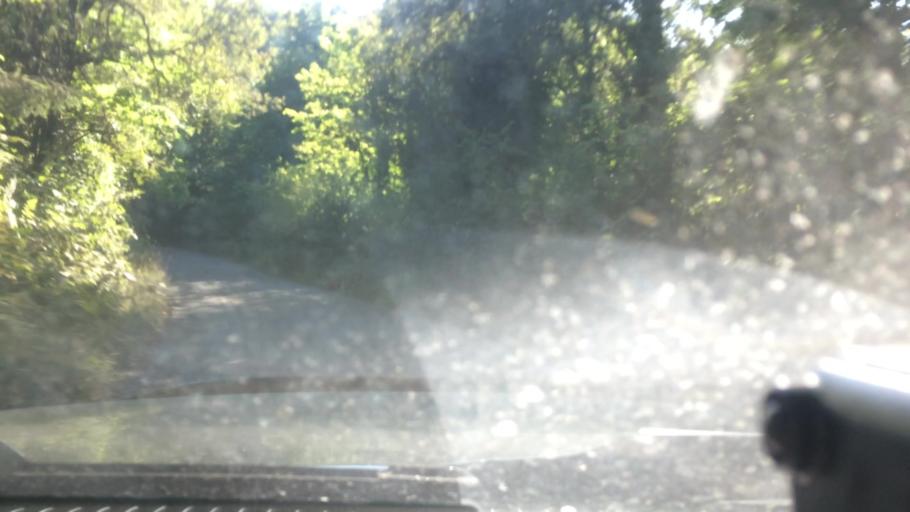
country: US
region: Oregon
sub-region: Yamhill County
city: Newberg
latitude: 45.3568
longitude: -122.9721
